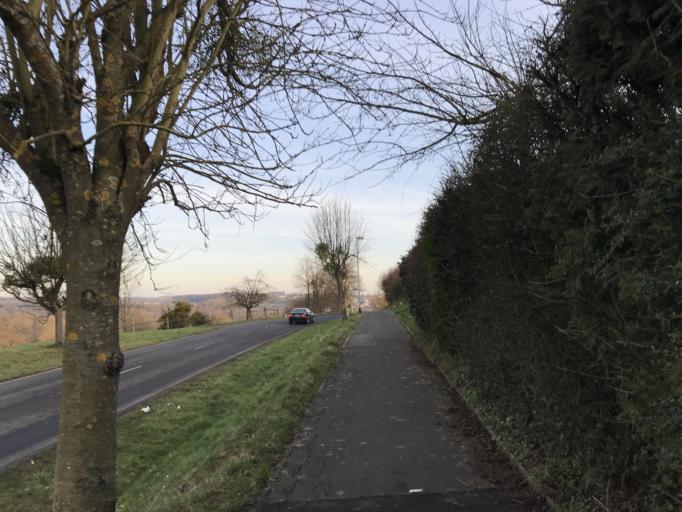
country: DE
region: Hesse
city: Weilburg
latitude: 50.4959
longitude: 8.2583
